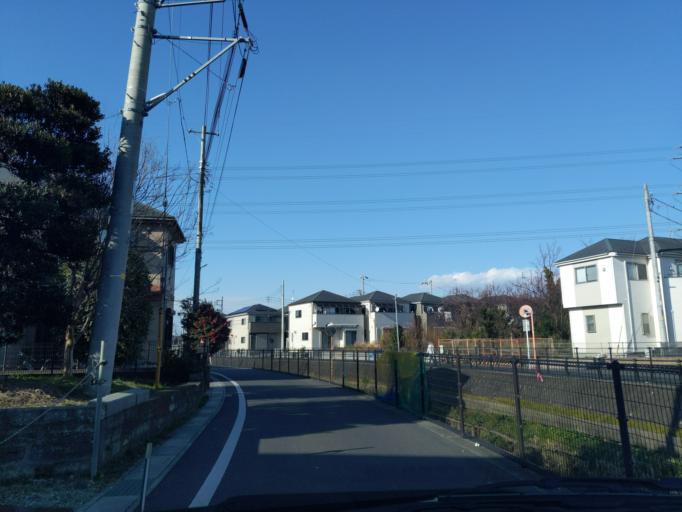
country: JP
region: Saitama
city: Soka
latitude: 35.8294
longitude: 139.7833
